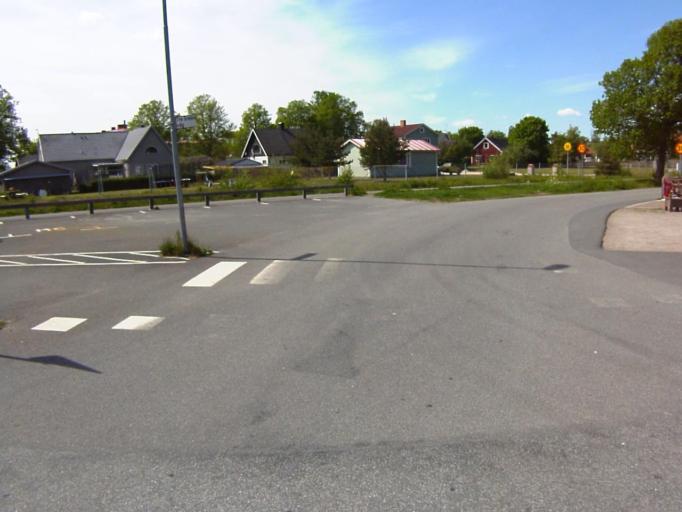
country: SE
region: Skane
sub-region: Kristianstads Kommun
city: Onnestad
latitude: 56.0744
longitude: 14.0877
